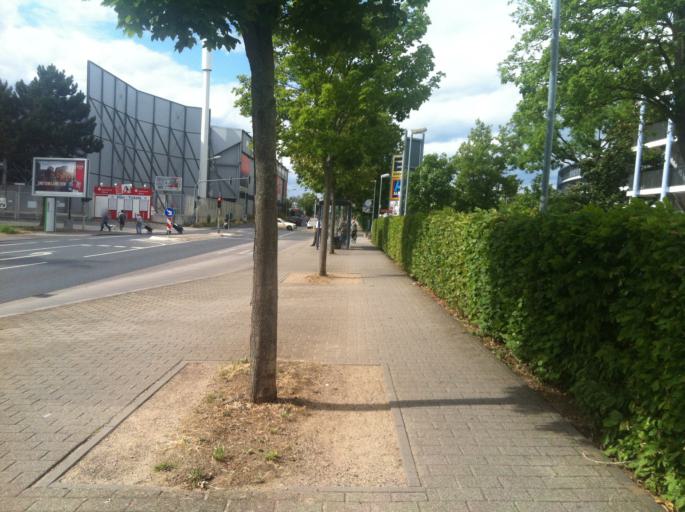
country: DE
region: Rheinland-Pfalz
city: Mainz
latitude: 49.9996
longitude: 8.2470
